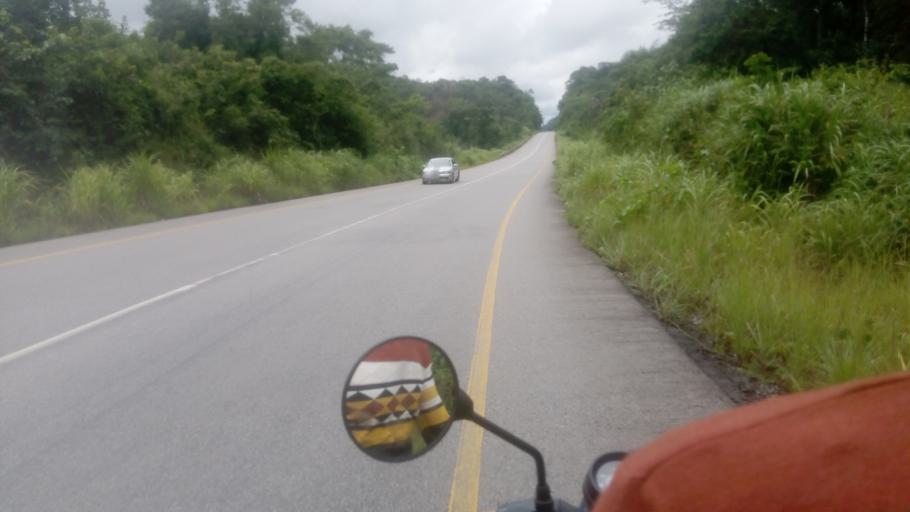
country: SL
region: Northern Province
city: Masaka
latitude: 8.6461
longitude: -11.7487
